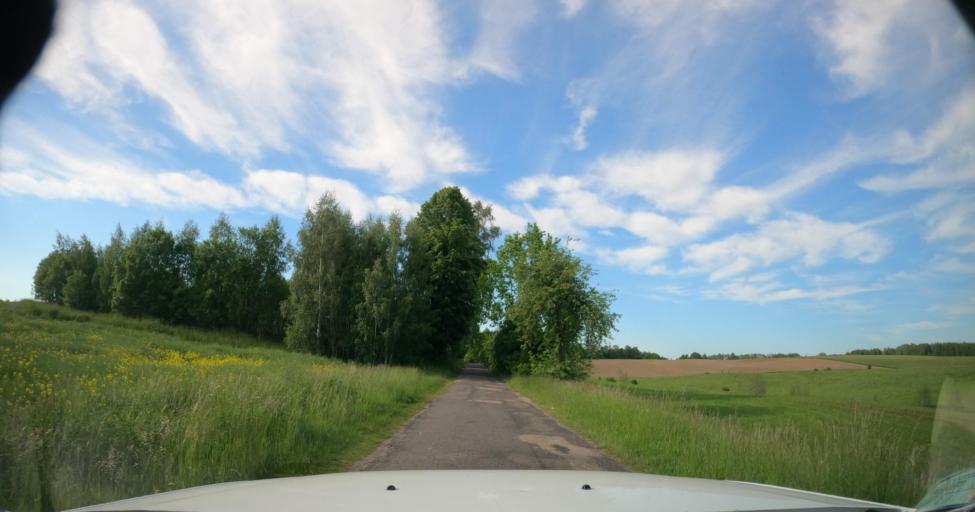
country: PL
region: Warmian-Masurian Voivodeship
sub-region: Powiat ostrodzki
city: Morag
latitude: 54.0545
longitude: 19.8892
